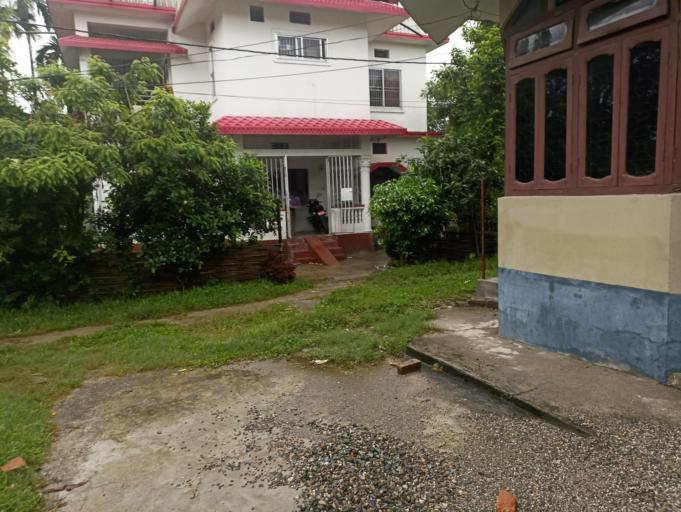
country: NP
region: Eastern Region
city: Ithari
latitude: 26.6025
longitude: 87.1563
